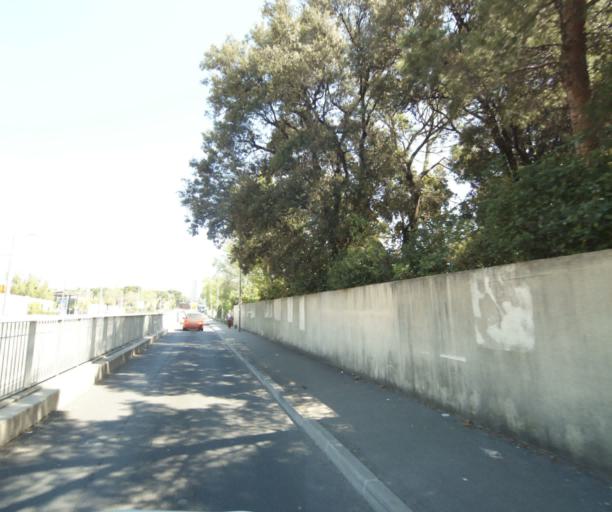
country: FR
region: Languedoc-Roussillon
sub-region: Departement de l'Herault
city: Juvignac
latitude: 43.6141
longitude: 3.8394
